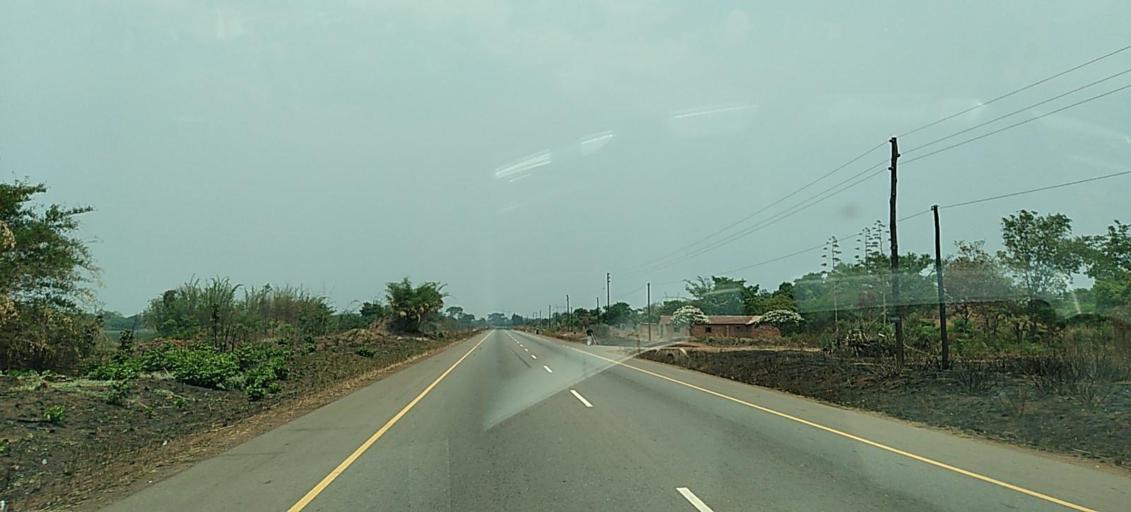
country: ZM
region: Copperbelt
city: Chingola
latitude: -12.5395
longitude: 27.6085
